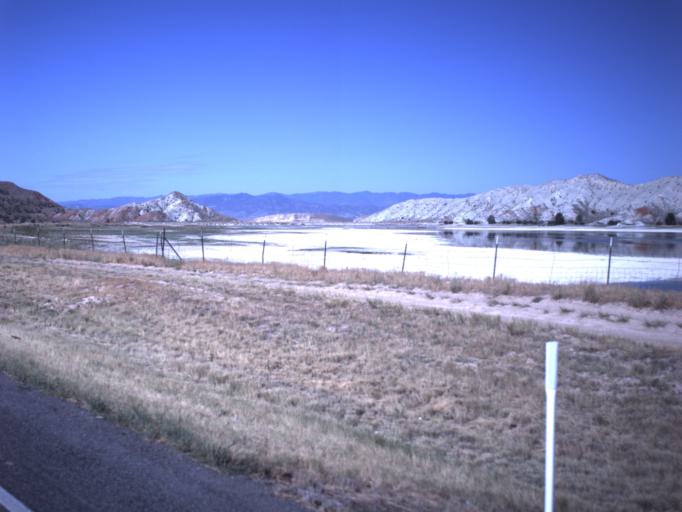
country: US
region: Utah
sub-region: Sanpete County
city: Manti
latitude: 39.1740
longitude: -111.7032
